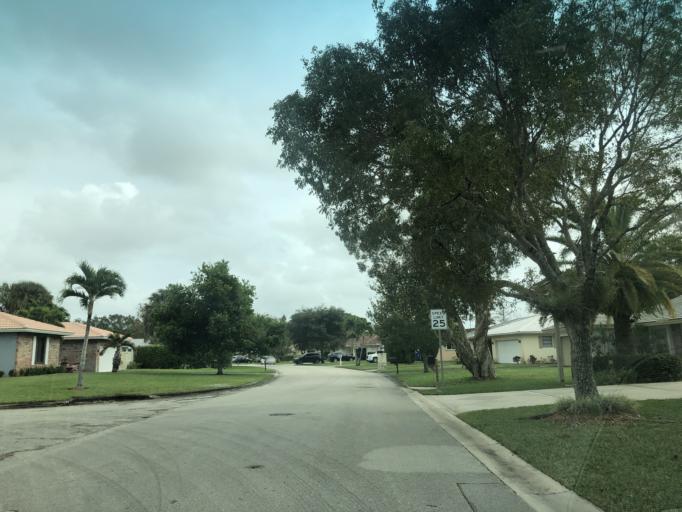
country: US
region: Florida
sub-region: Broward County
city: Margate
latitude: 26.2485
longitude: -80.2401
